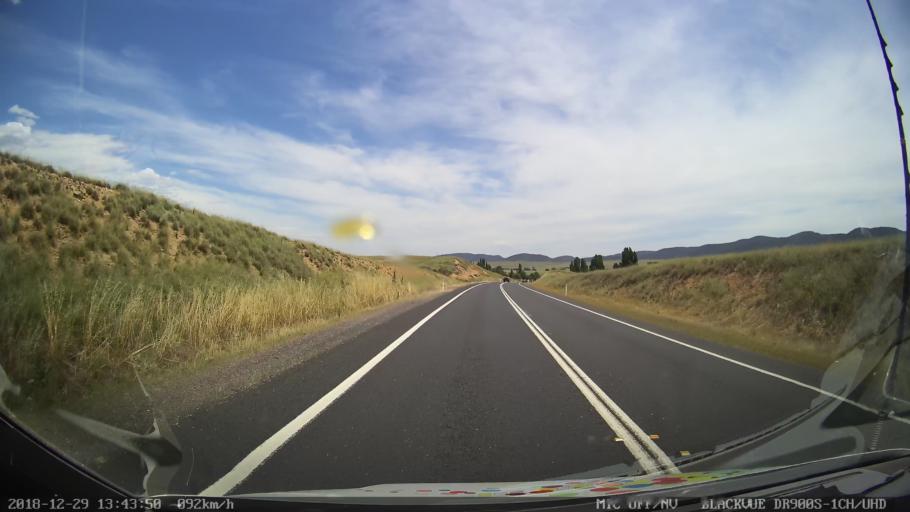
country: AU
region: New South Wales
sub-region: Cooma-Monaro
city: Cooma
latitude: -36.0783
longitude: 149.1594
